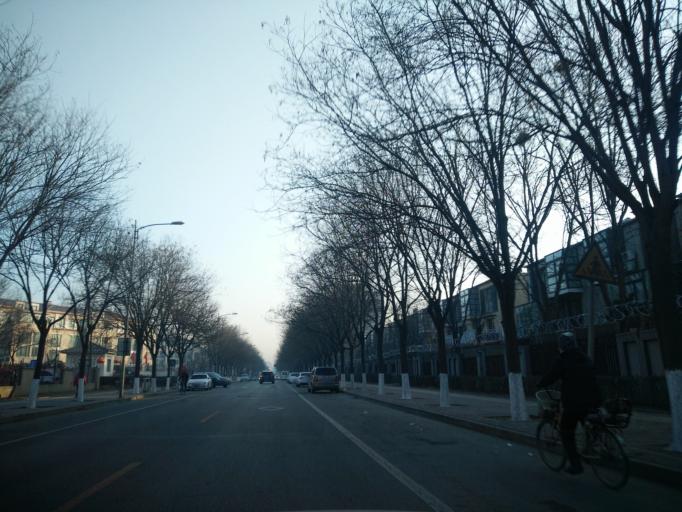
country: CN
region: Beijing
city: Jiugong
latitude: 39.7871
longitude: 116.4852
